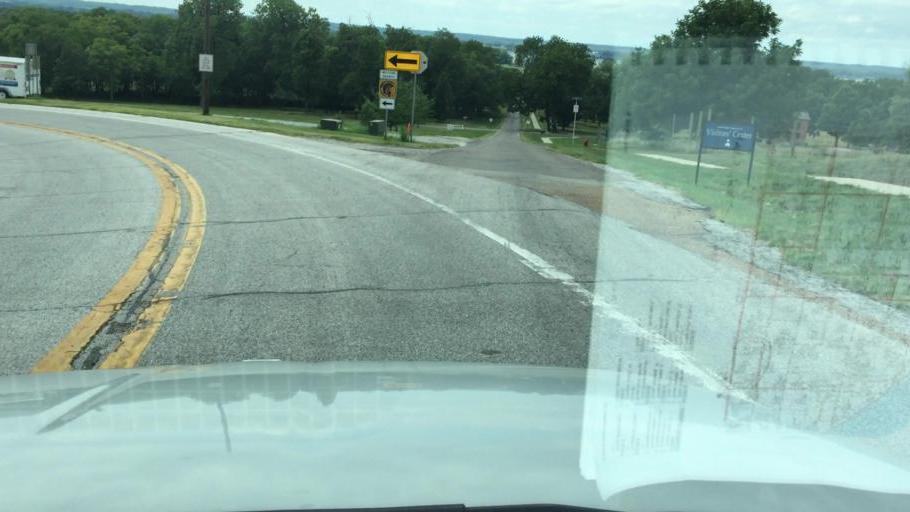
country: US
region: Illinois
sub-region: Hancock County
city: Nauvoo
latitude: 40.5498
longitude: -91.3860
